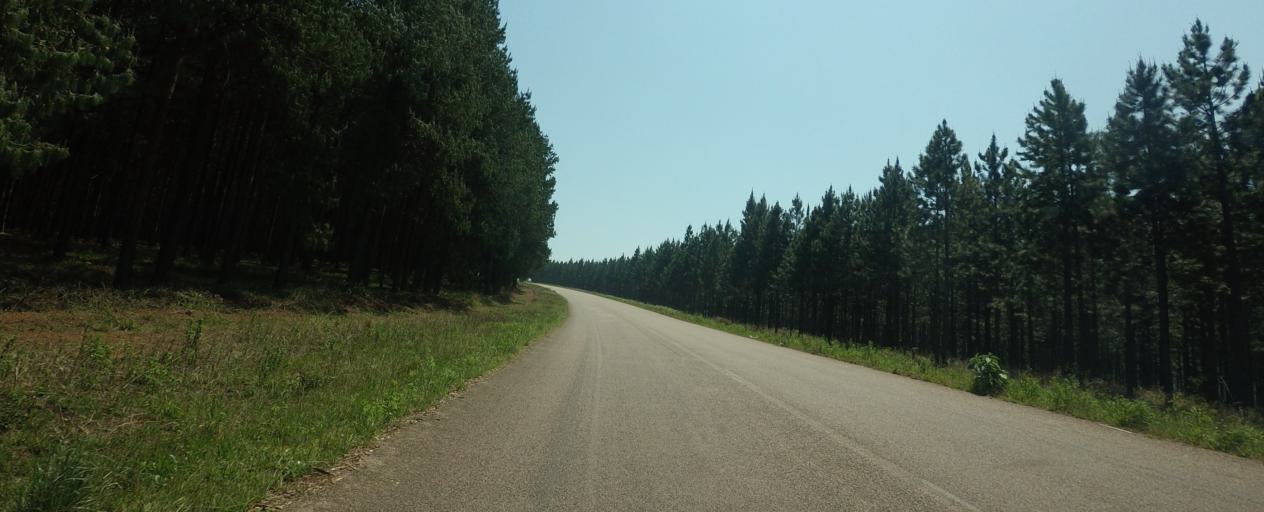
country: ZA
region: Mpumalanga
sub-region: Ehlanzeni District
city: Graksop
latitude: -25.0521
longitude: 30.8188
